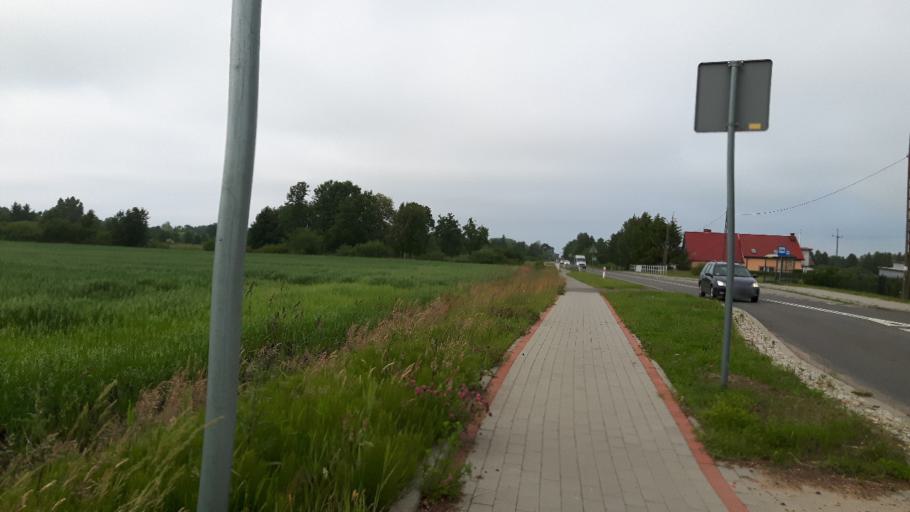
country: PL
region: West Pomeranian Voivodeship
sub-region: Powiat koszalinski
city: Sianow
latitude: 54.3241
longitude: 16.3098
